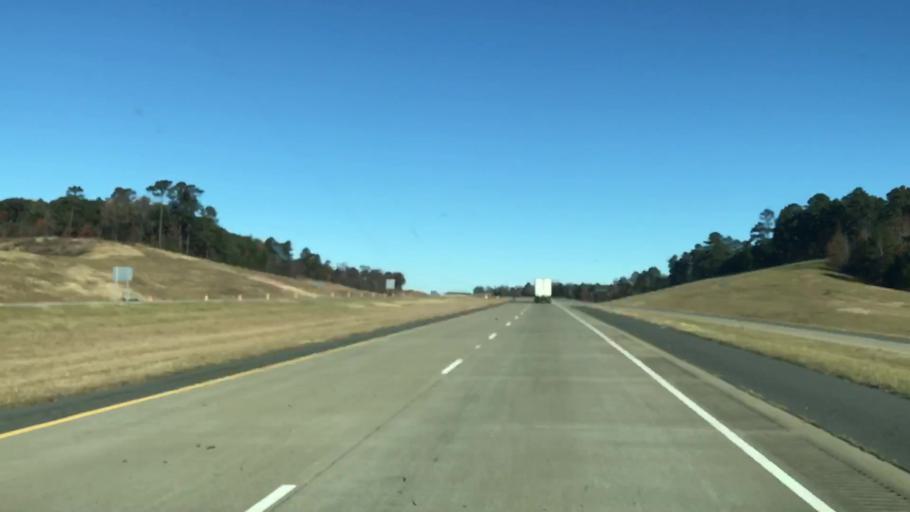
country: US
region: Louisiana
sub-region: Caddo Parish
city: Vivian
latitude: 32.9451
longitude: -93.8979
